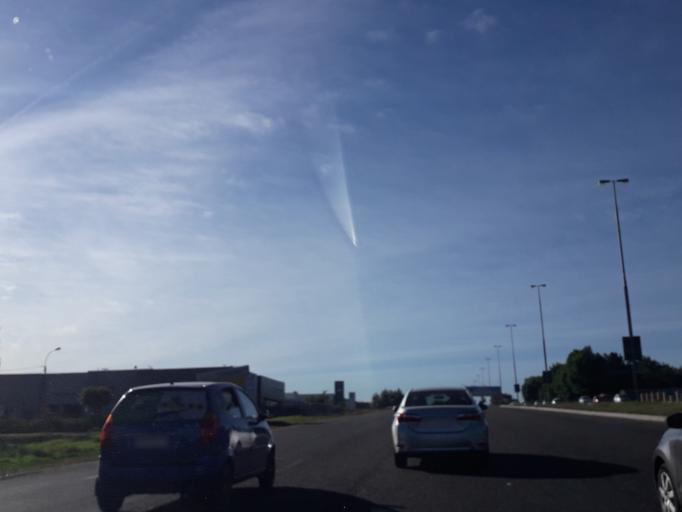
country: ZA
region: Gauteng
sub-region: City of Johannesburg Metropolitan Municipality
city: Roodepoort
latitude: -26.1347
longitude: 27.9154
